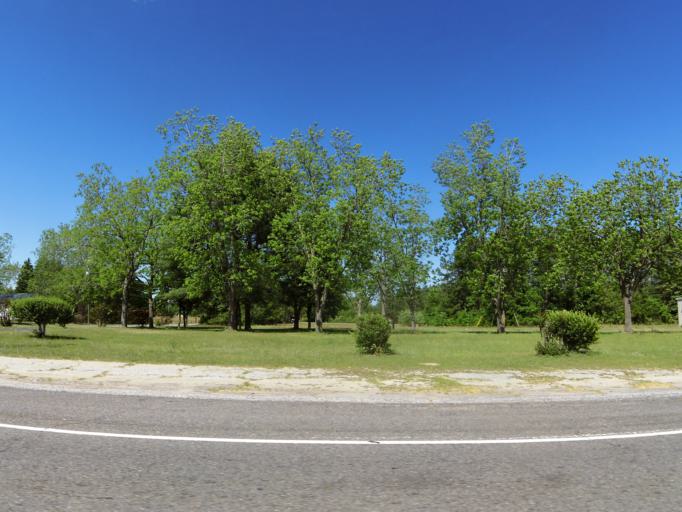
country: US
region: South Carolina
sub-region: Barnwell County
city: Williston
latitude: 33.4859
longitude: -81.5181
